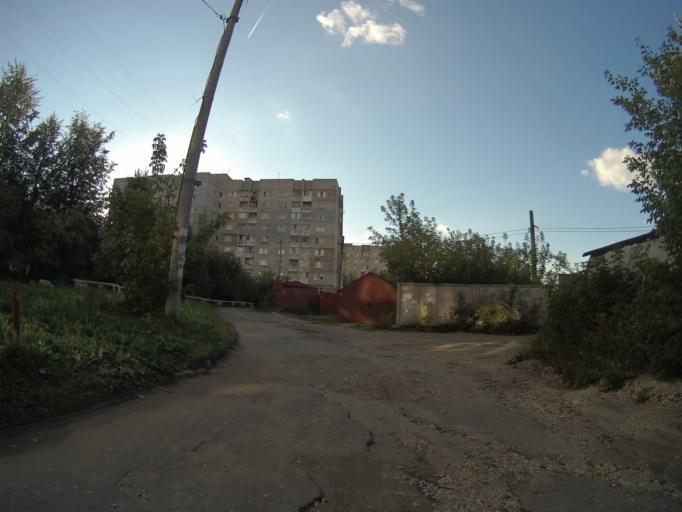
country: RU
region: Vladimir
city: Vladimir
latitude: 56.1536
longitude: 40.3758
